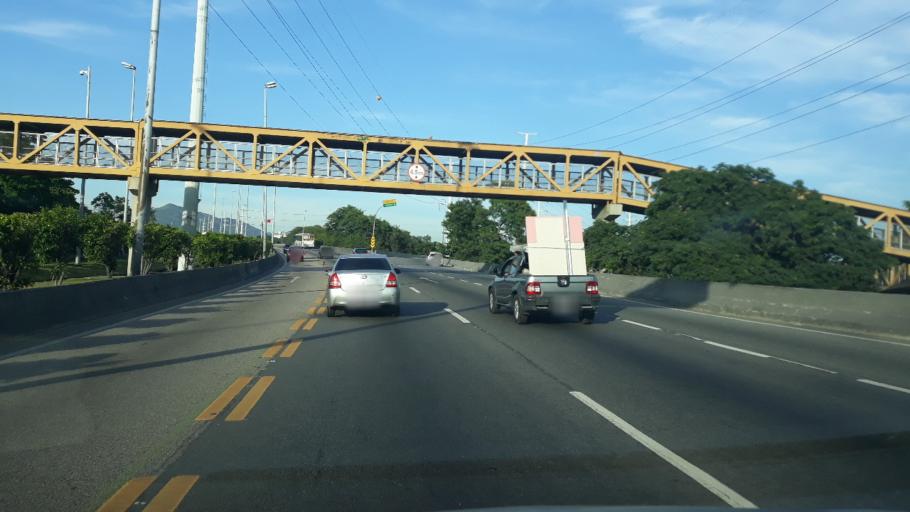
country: BR
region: Rio de Janeiro
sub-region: Rio De Janeiro
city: Rio de Janeiro
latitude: -22.8716
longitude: -43.2646
